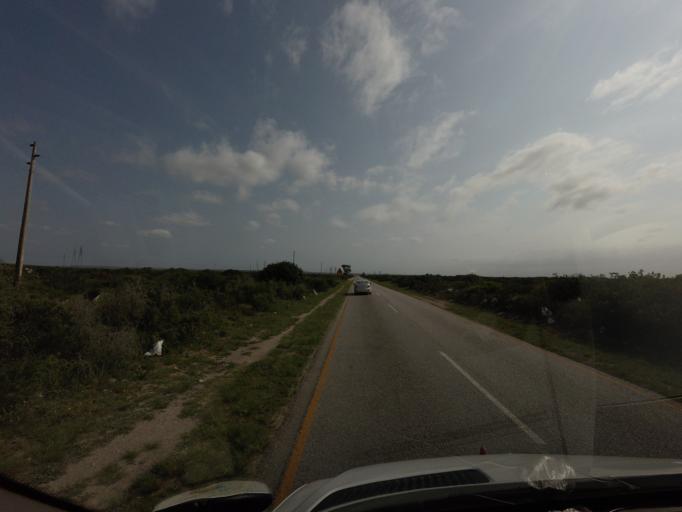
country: ZA
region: Eastern Cape
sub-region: Nelson Mandela Bay Metropolitan Municipality
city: Port Elizabeth
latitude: -33.7639
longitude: 25.5934
